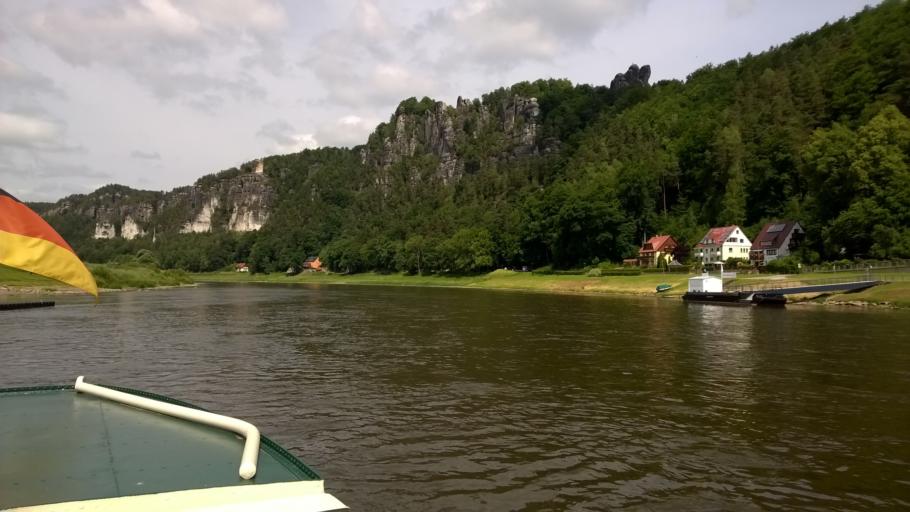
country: DE
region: Saxony
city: Hohnstein
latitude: 50.9575
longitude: 14.0797
